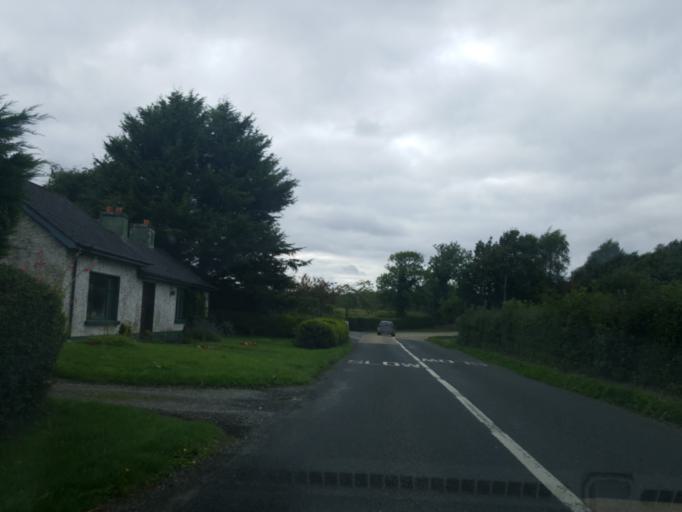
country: IE
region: Leinster
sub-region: Kildare
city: Kilcullen
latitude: 53.1264
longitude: -6.7411
